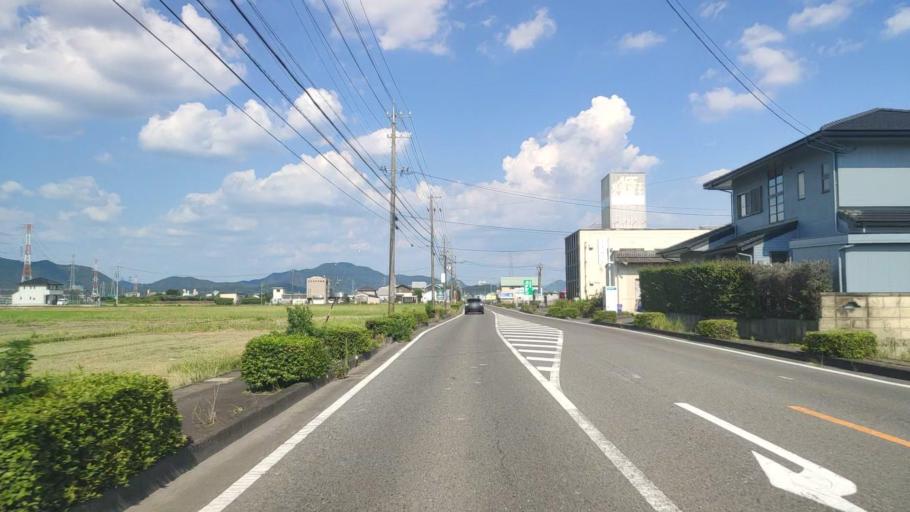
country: JP
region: Gifu
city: Gifu-shi
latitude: 35.4505
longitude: 136.7150
